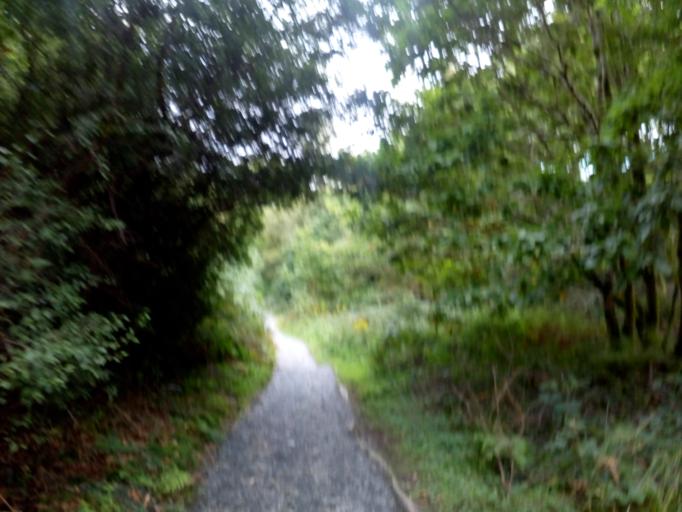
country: GB
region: Wales
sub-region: Gwynedd
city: Maentwrog
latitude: 52.9539
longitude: -4.0107
